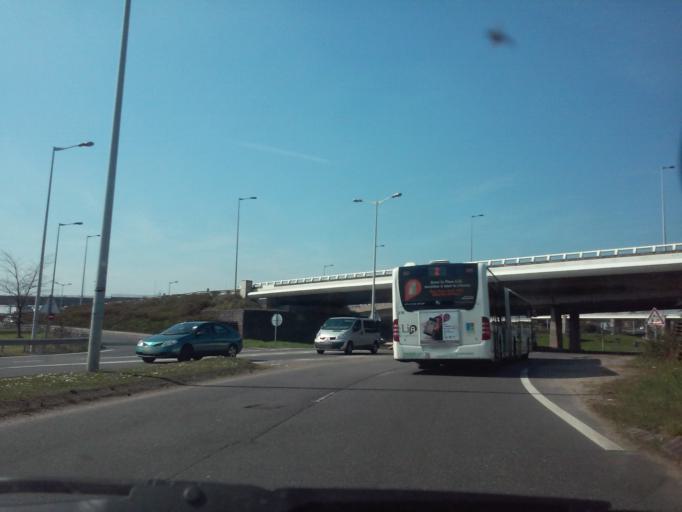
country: FR
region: Haute-Normandie
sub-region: Departement de la Seine-Maritime
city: Harfleur
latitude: 49.5043
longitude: 0.1949
